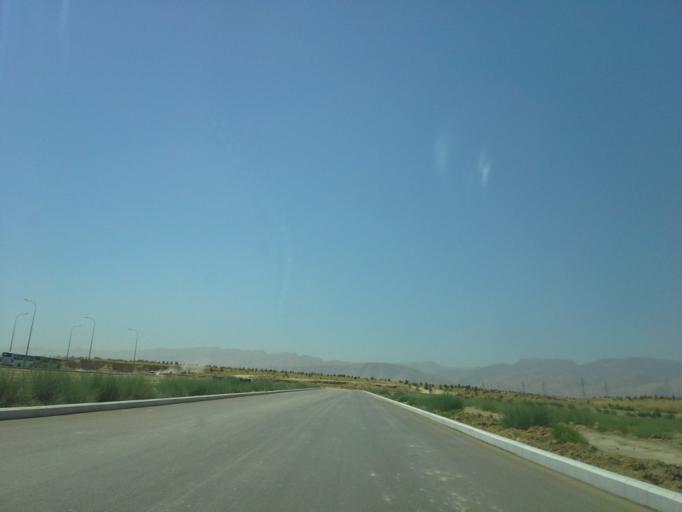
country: TM
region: Ahal
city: Ashgabat
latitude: 37.8874
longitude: 58.4046
